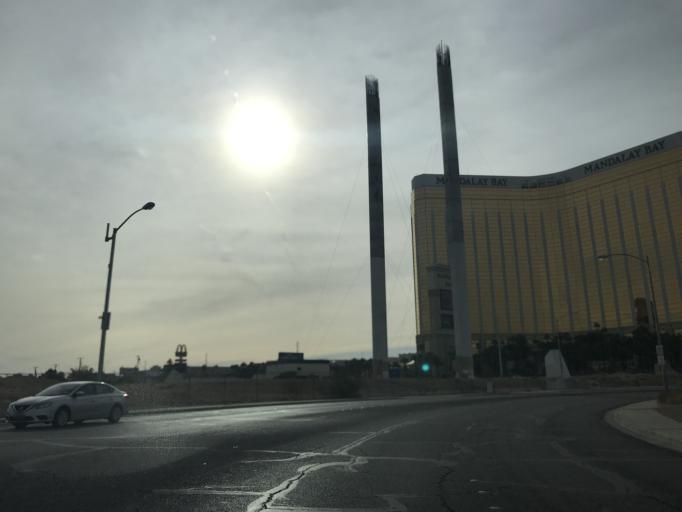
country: US
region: Nevada
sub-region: Clark County
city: Paradise
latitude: 36.0939
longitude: -115.1707
